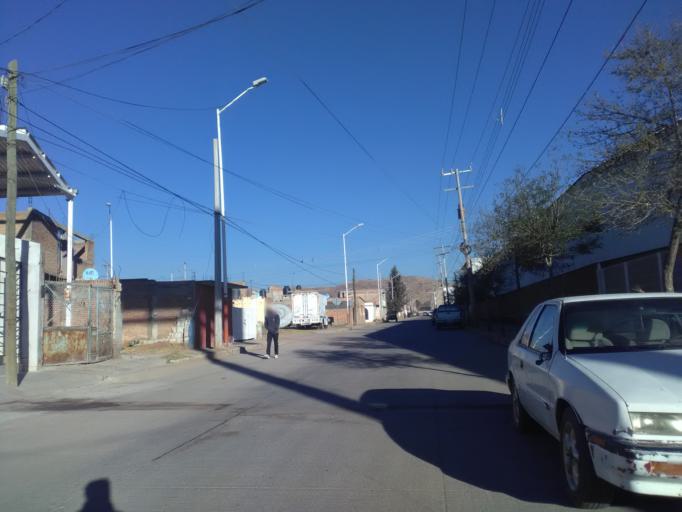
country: MX
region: Durango
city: Victoria de Durango
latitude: 24.0528
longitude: -104.6523
